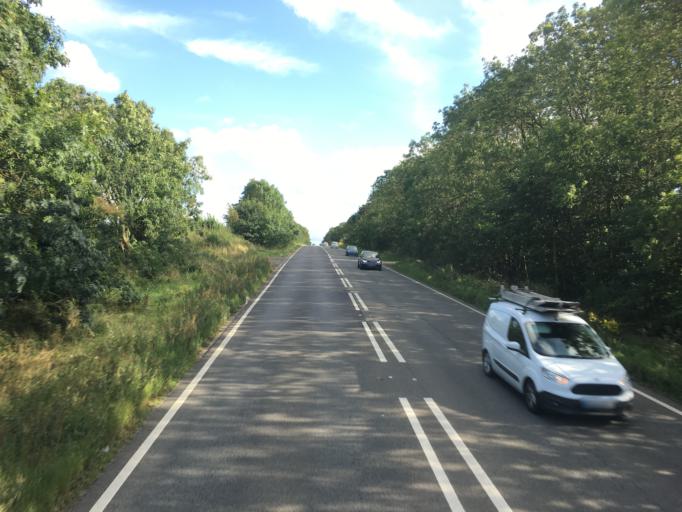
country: GB
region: England
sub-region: Leicestershire
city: Lutterworth
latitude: 52.4302
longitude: -1.2323
